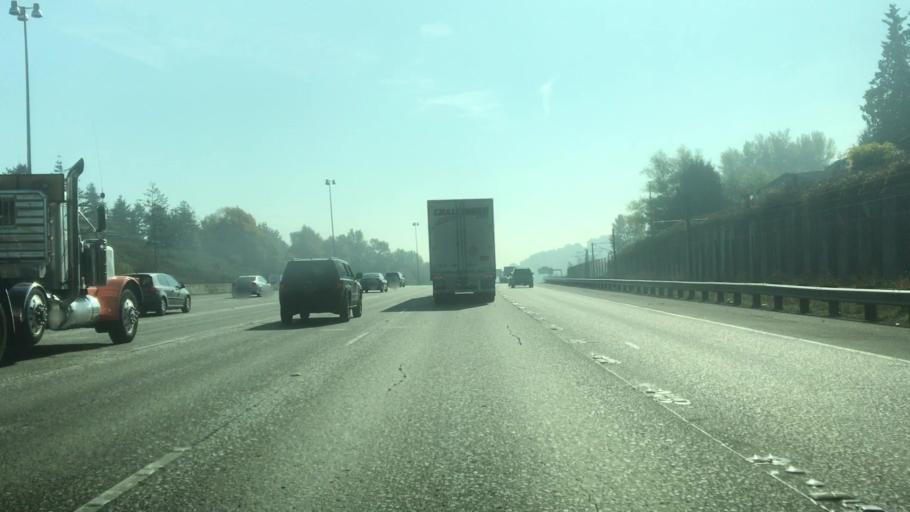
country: US
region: Washington
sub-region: King County
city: Tukwila
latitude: 47.4740
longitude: -122.2698
